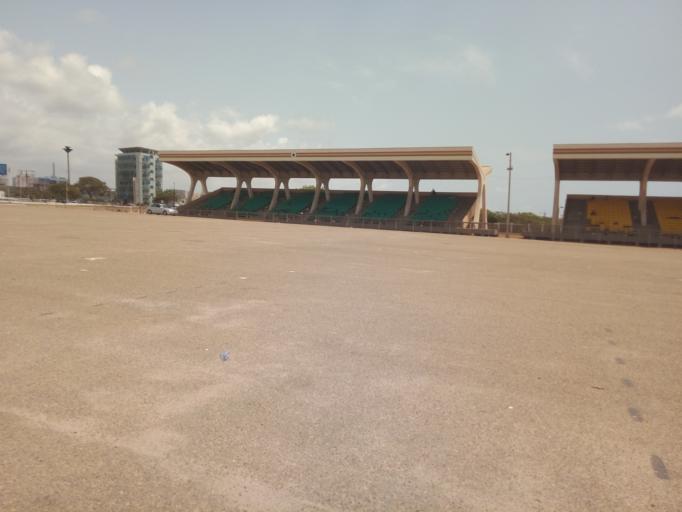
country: GH
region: Greater Accra
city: Accra
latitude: 5.5479
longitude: -0.1922
